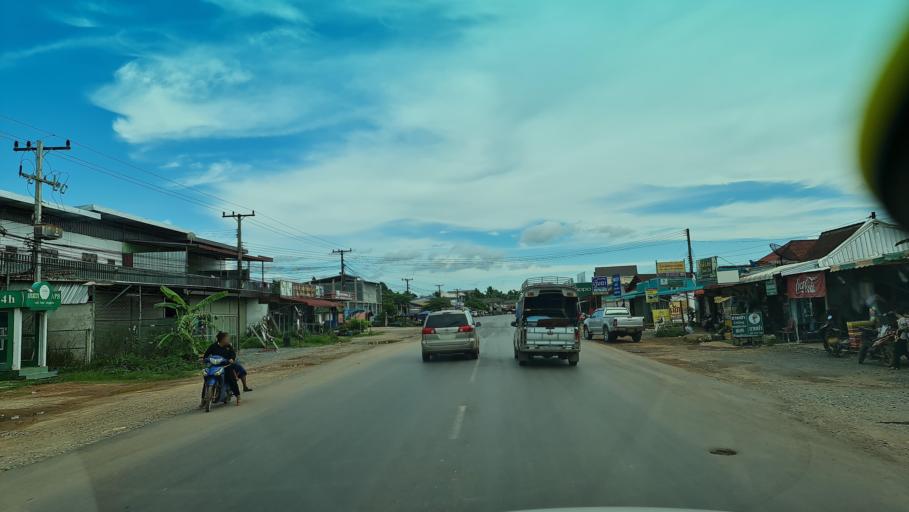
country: TH
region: Nakhon Phanom
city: Ban Phaeng
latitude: 18.1012
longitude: 104.2851
